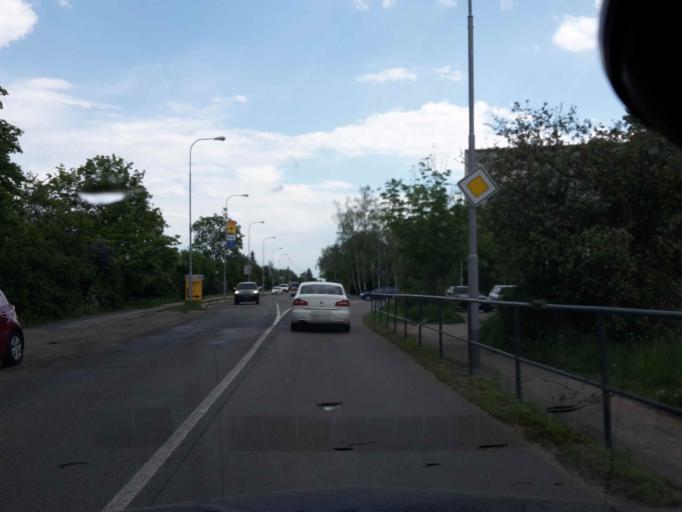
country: CZ
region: South Moravian
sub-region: Mesto Brno
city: Brno
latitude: 49.2350
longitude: 16.6285
